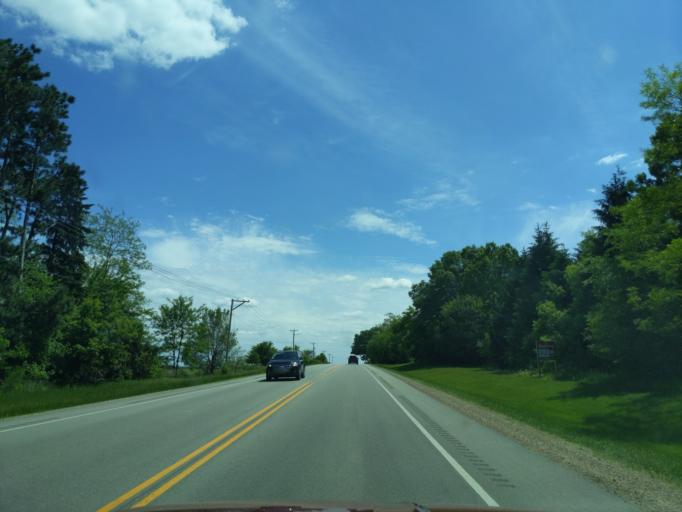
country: US
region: Wisconsin
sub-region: Columbia County
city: Pardeeville
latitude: 43.4768
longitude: -89.3151
